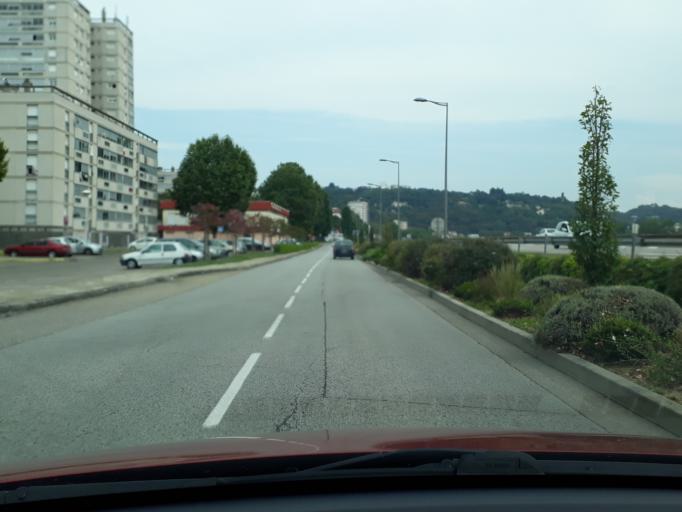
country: FR
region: Rhone-Alpes
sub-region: Departement du Rhone
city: Saint-Romain-en-Gal
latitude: 45.5404
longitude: 4.8583
